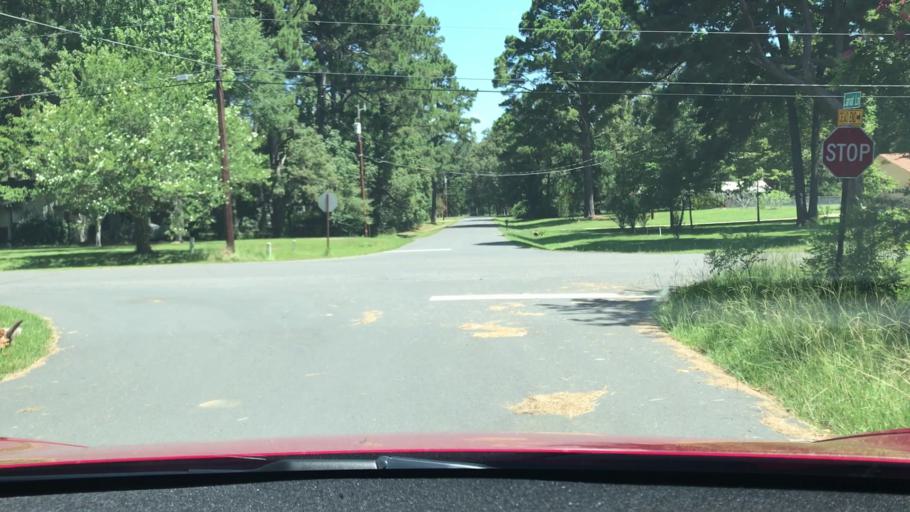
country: US
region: Louisiana
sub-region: De Soto Parish
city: Stonewall
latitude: 32.3446
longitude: -93.7085
